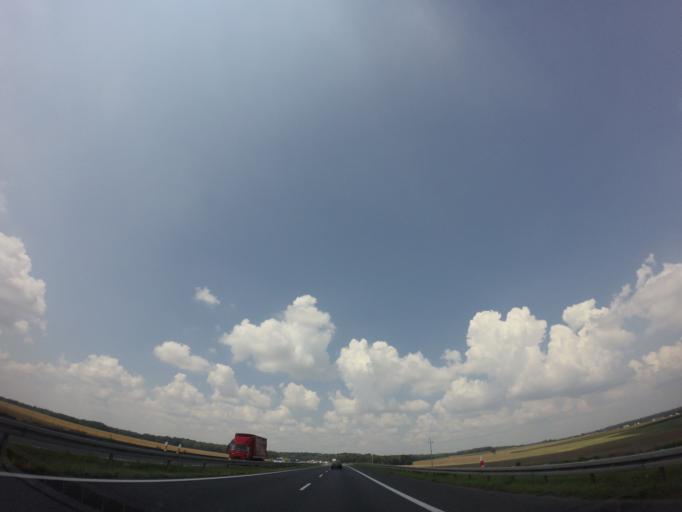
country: PL
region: Opole Voivodeship
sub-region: Powiat strzelecki
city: Ujazd
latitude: 50.4191
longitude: 18.4002
